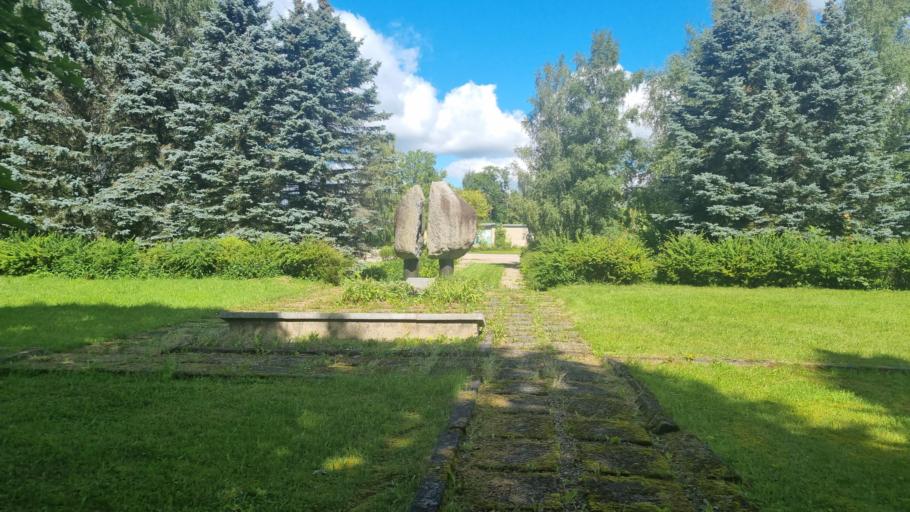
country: LV
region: Daugavpils
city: Daugavpils
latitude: 55.7250
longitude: 26.5511
